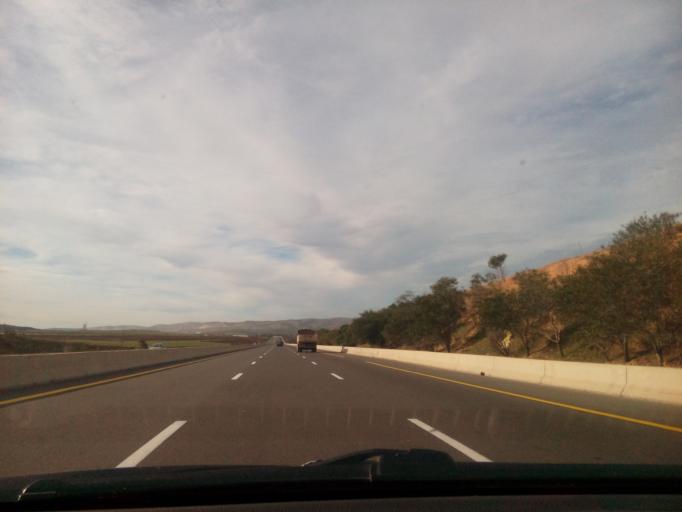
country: DZ
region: Mascara
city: Sig
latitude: 35.5103
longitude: -0.3668
